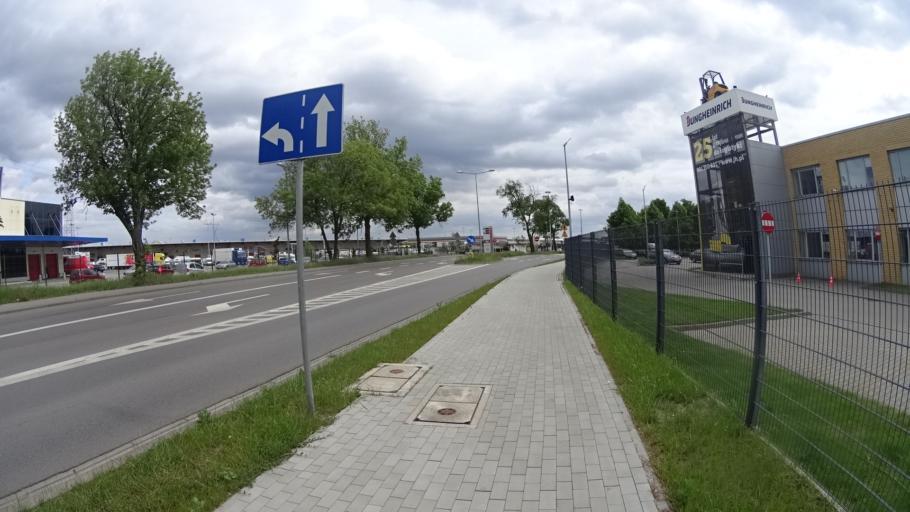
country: PL
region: Masovian Voivodeship
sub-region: Powiat warszawski zachodni
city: Babice
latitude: 52.2201
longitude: 20.8378
